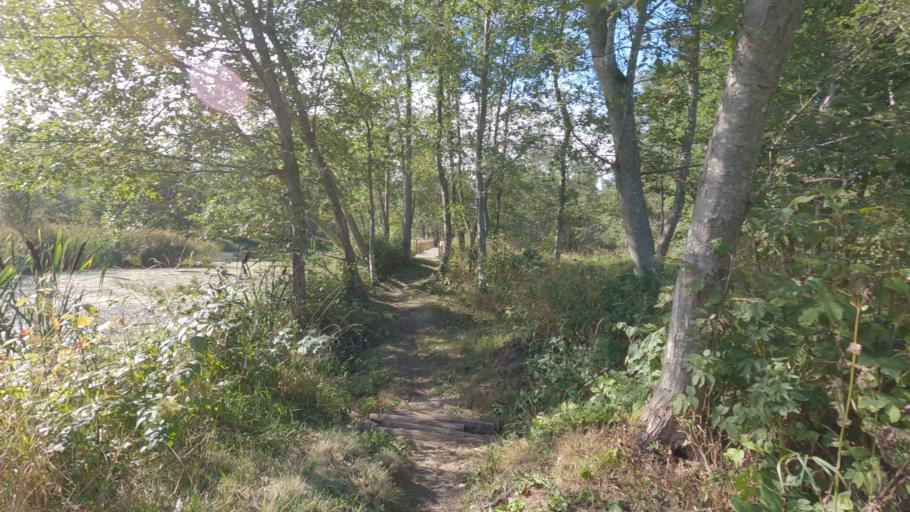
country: EE
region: Raplamaa
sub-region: Rapla vald
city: Rapla
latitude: 58.9997
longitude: 24.8199
